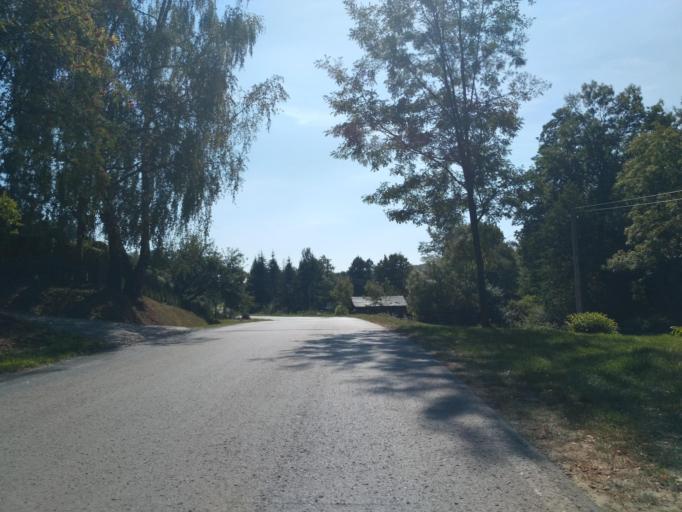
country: PL
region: Subcarpathian Voivodeship
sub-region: Powiat brzozowski
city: Niebocko
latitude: 49.6597
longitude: 22.1324
